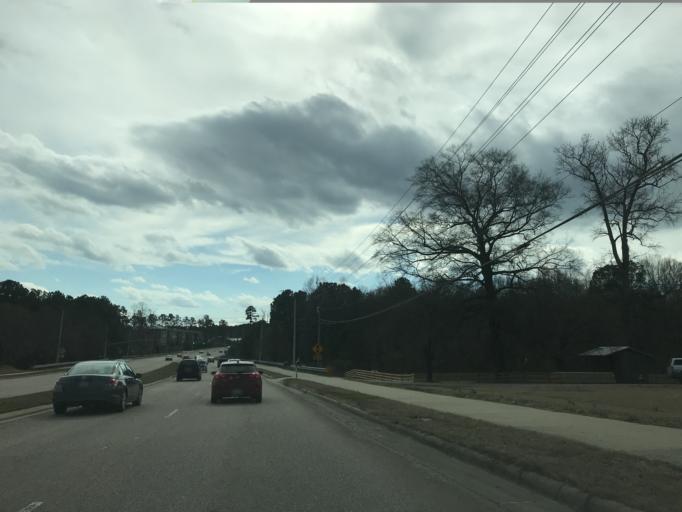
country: US
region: North Carolina
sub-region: Wake County
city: Morrisville
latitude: 35.8188
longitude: -78.8478
